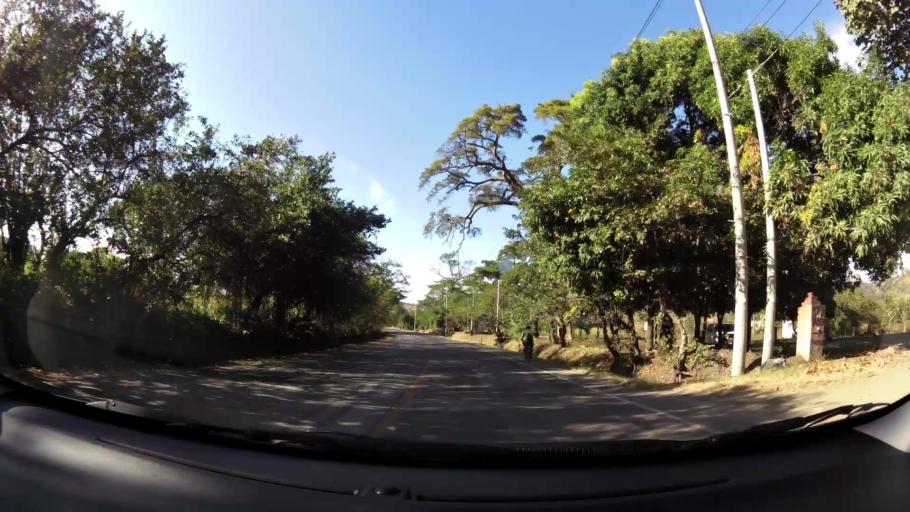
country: SV
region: Santa Ana
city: Texistepeque
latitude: 14.1287
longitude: -89.5005
